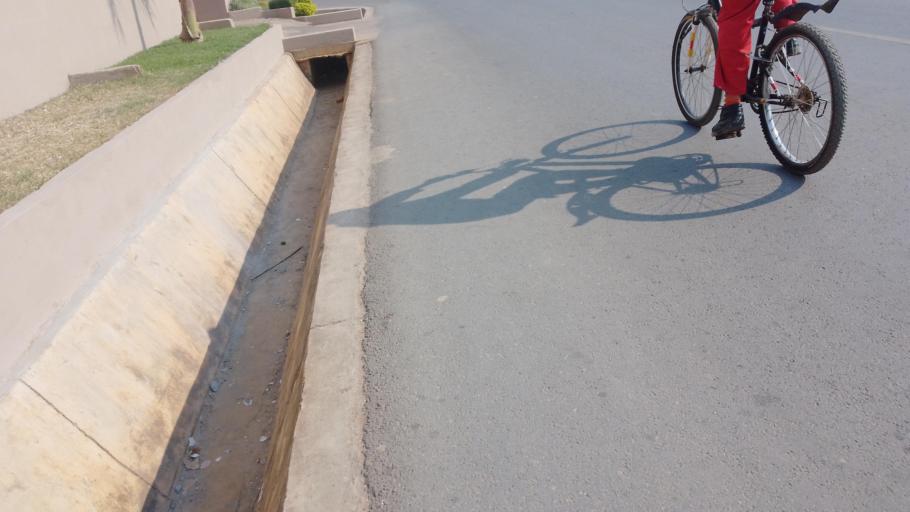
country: ZM
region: Lusaka
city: Lusaka
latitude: -15.3917
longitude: 28.3872
